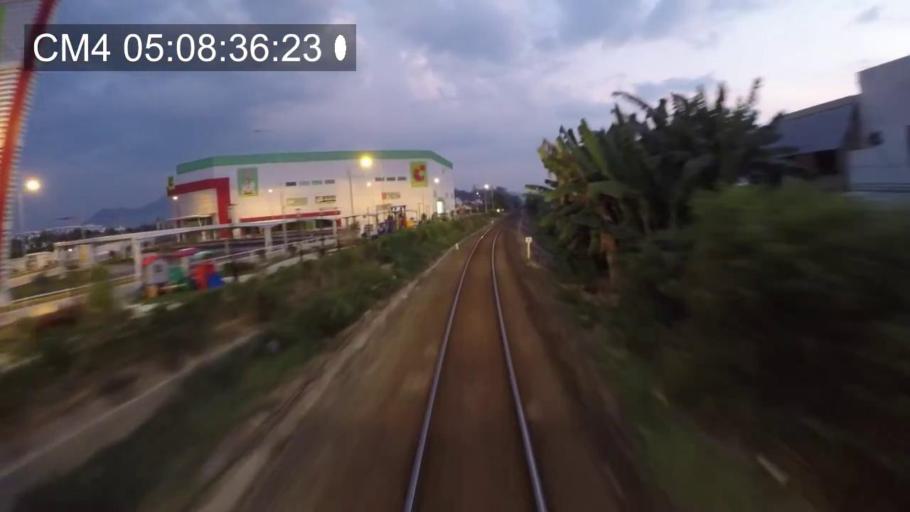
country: VN
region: Khanh Hoa
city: Nha Trang
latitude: 12.2940
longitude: 109.1865
